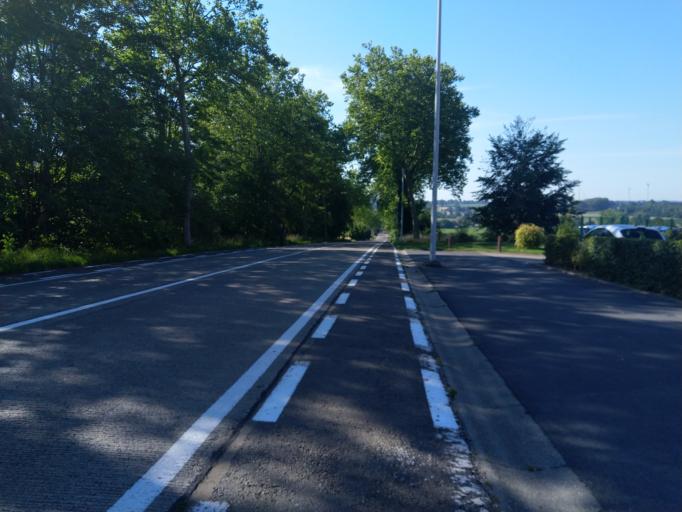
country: BE
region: Wallonia
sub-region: Province du Hainaut
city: Chasse Royale
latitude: 50.4138
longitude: 3.9550
